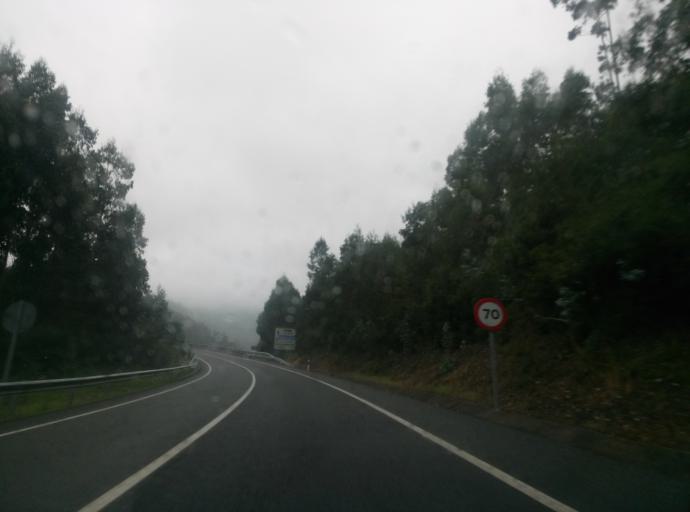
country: ES
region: Galicia
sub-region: Provincia de Lugo
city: Viveiro
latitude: 43.5580
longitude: -7.6483
